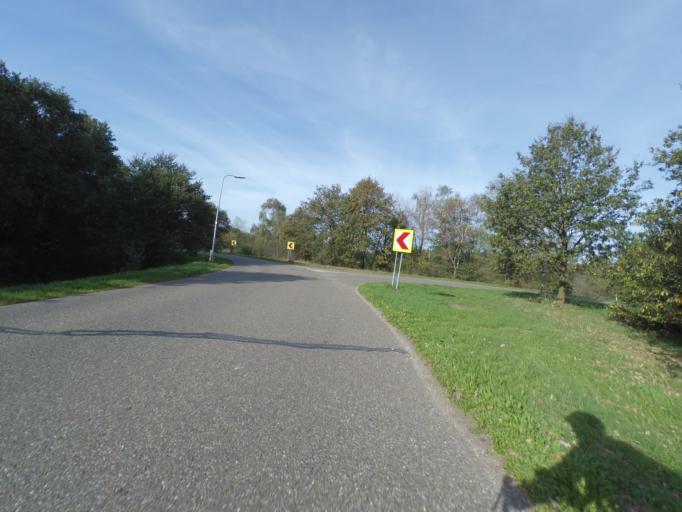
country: NL
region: Gelderland
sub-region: Gemeente Lochem
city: Epse
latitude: 52.2389
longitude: 6.2395
